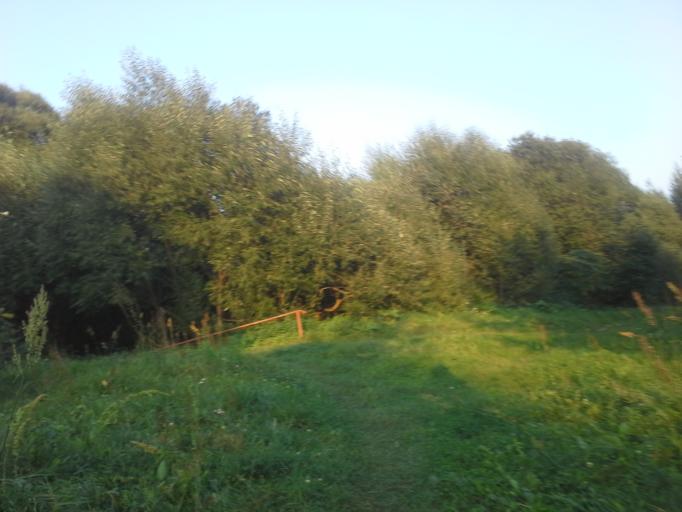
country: RU
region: Moskovskaya
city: Dubrovitsy
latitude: 55.5038
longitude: 37.4382
